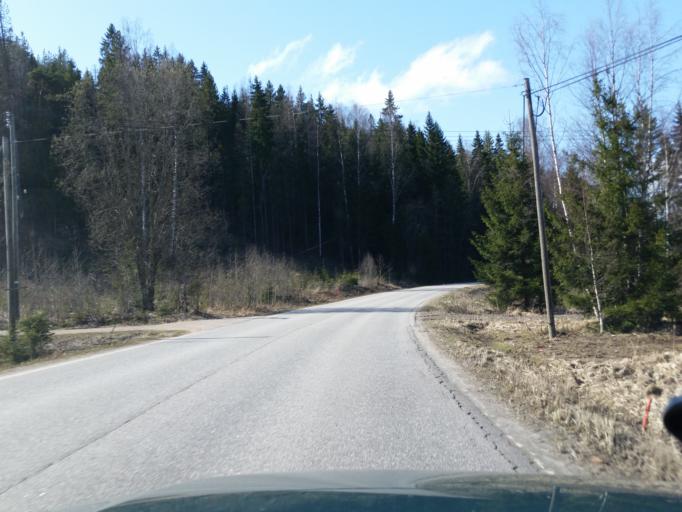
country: FI
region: Uusimaa
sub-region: Helsinki
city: Vihti
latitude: 60.4253
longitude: 24.2581
